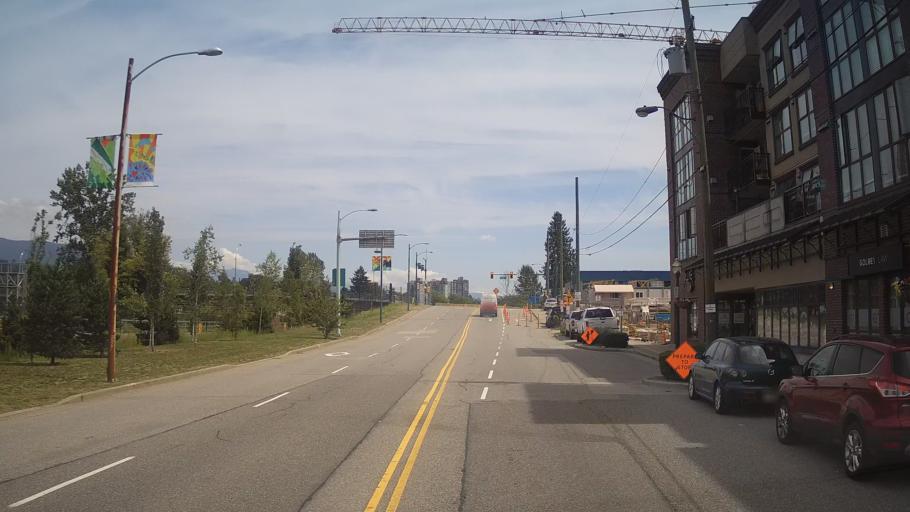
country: CA
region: British Columbia
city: Port Moody
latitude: 49.2777
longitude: -122.8520
